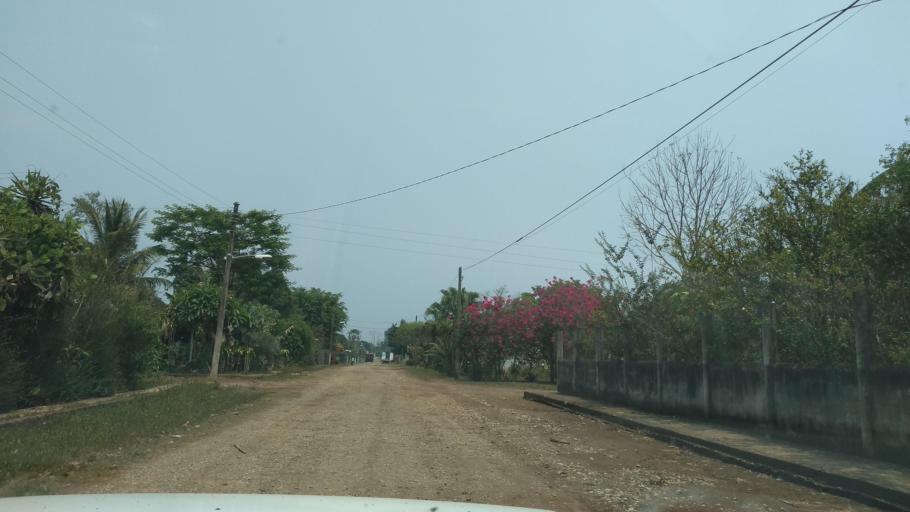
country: MX
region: Veracruz
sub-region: Tezonapa
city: Laguna Chica (Pueblo Nuevo)
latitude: 18.5323
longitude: -96.7645
